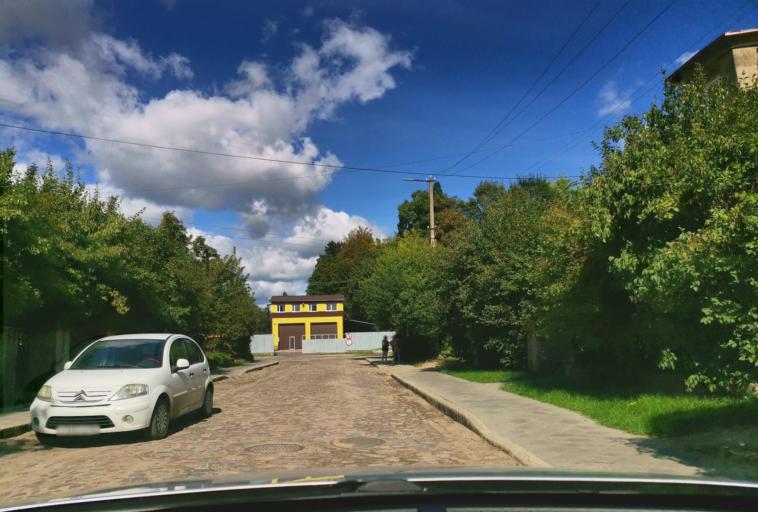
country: RU
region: Kaliningrad
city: Chernyakhovsk
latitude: 54.6376
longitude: 21.8394
